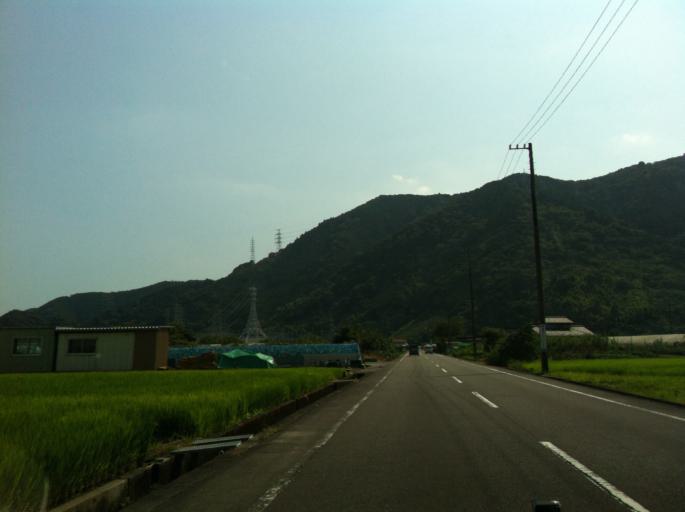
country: JP
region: Shizuoka
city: Shizuoka-shi
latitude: 35.0695
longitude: 138.3635
